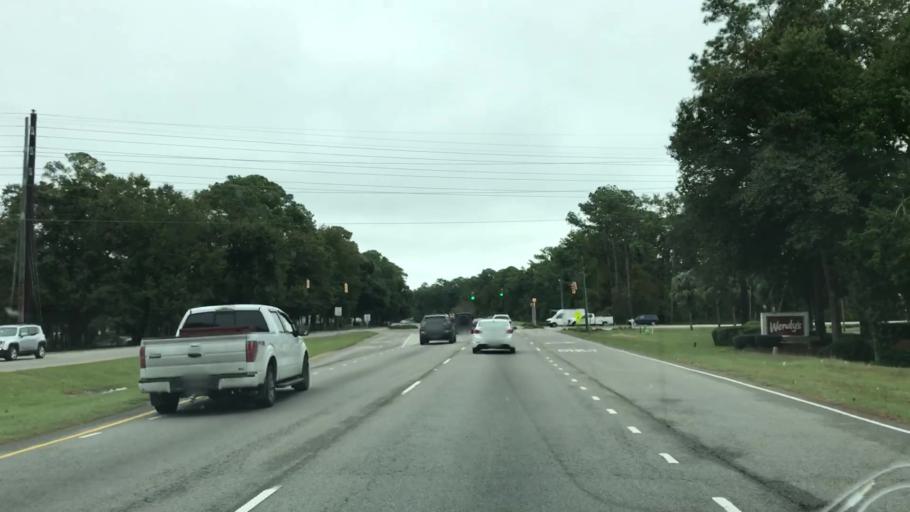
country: US
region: South Carolina
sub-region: Beaufort County
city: Hilton Head Island
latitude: 32.2135
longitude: -80.7306
